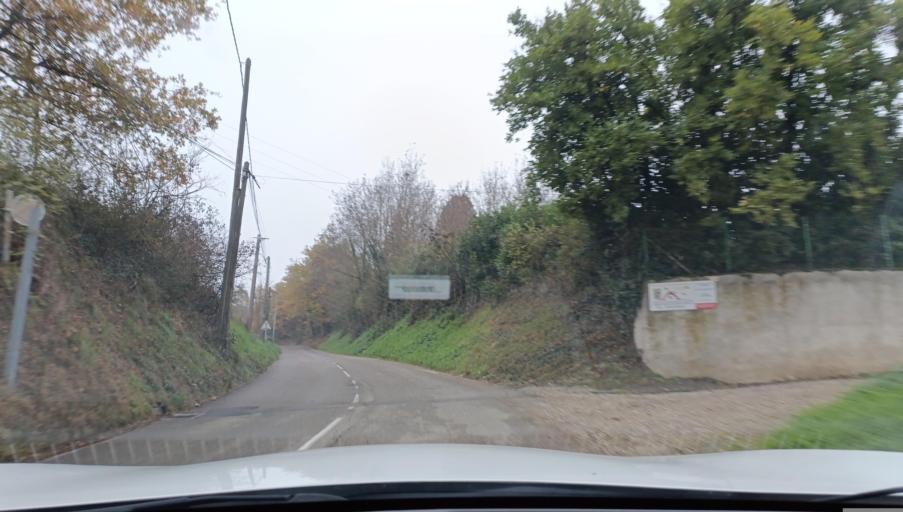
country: FR
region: Rhone-Alpes
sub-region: Departement de l'Isere
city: Serpaize
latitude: 45.5482
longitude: 4.9211
